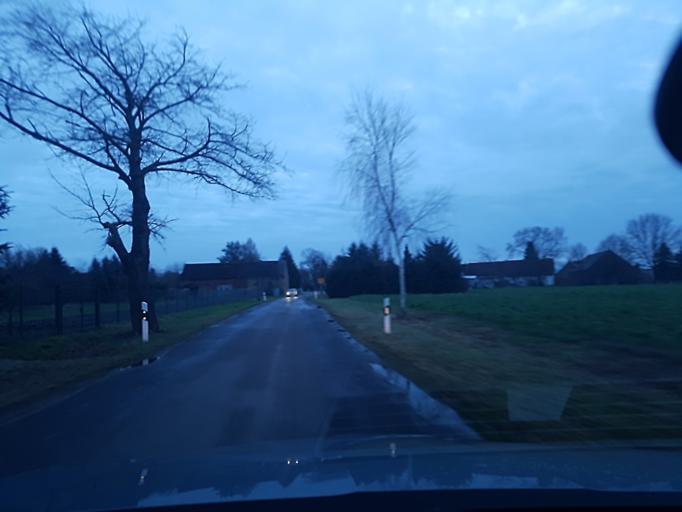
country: DE
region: Brandenburg
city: Finsterwalde
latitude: 51.6069
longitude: 13.6705
